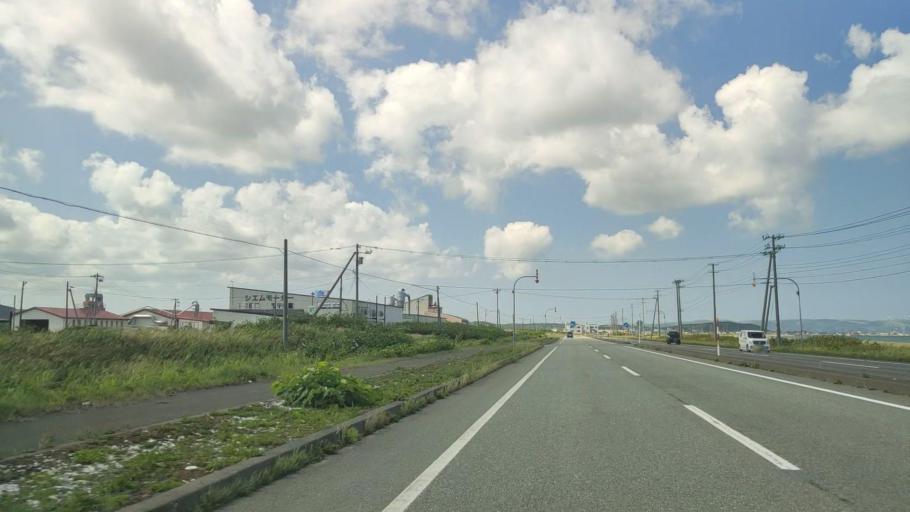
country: JP
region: Hokkaido
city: Makubetsu
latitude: 45.4042
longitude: 141.7899
